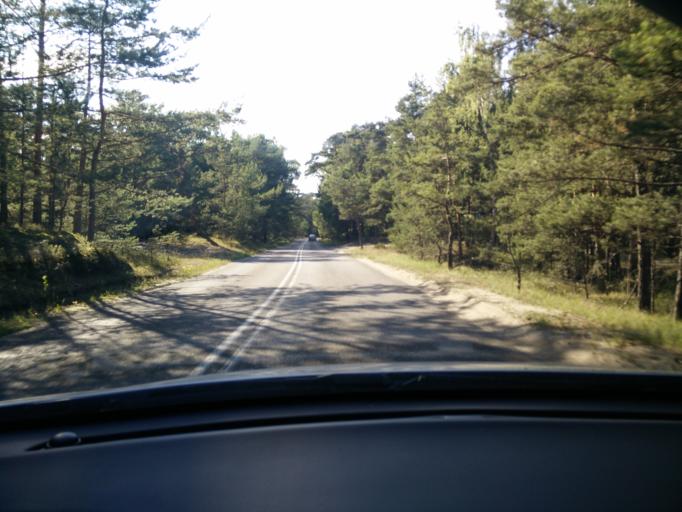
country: PL
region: Pomeranian Voivodeship
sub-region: Powiat pucki
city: Hel
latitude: 54.6274
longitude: 18.7929
